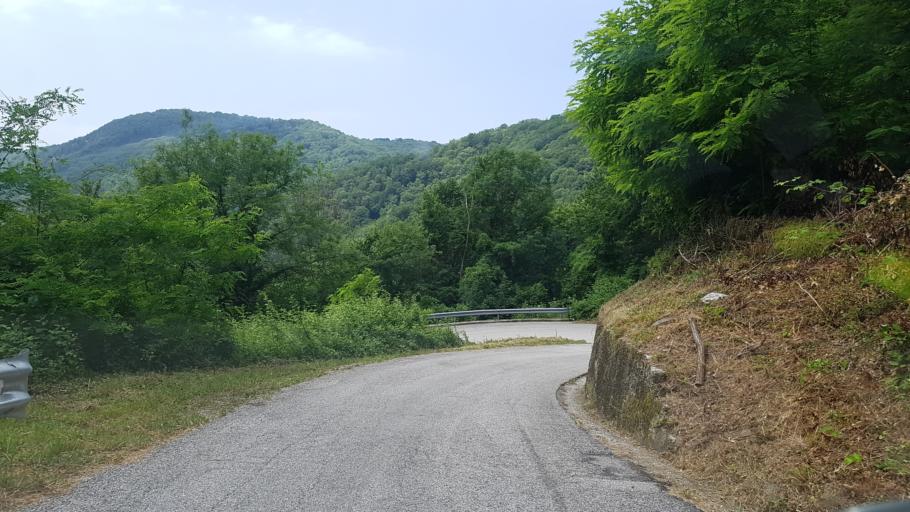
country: IT
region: Friuli Venezia Giulia
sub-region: Provincia di Udine
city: Torreano
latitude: 46.1676
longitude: 13.4318
